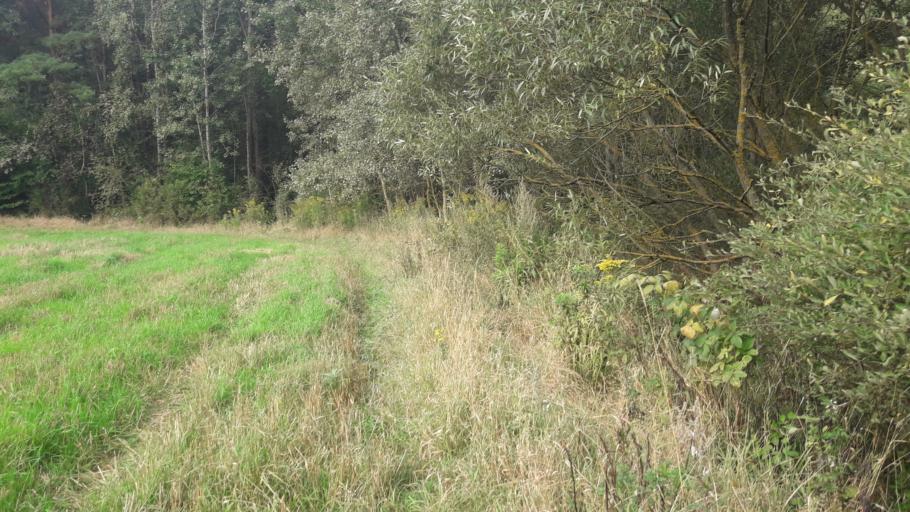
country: BY
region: Minsk
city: Pyatryshki
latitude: 54.1369
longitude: 27.1334
